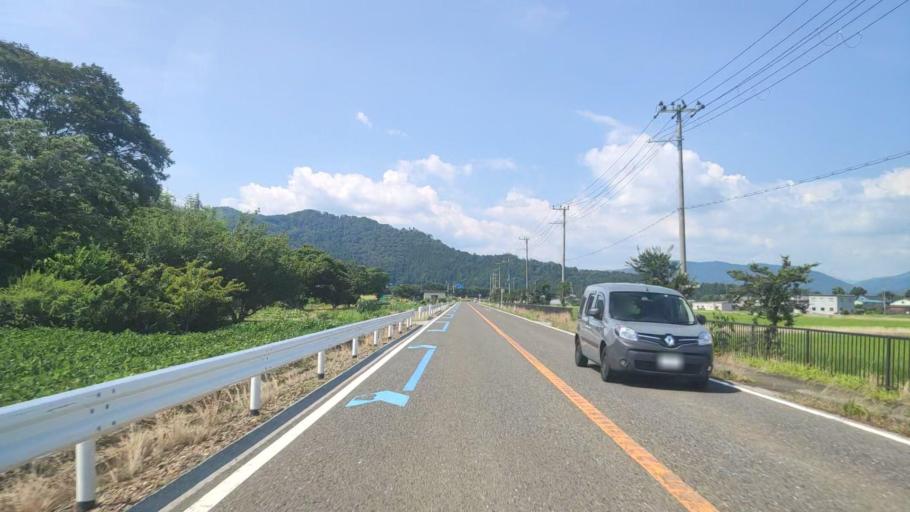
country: JP
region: Shiga Prefecture
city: Nagahama
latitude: 35.4640
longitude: 136.2064
